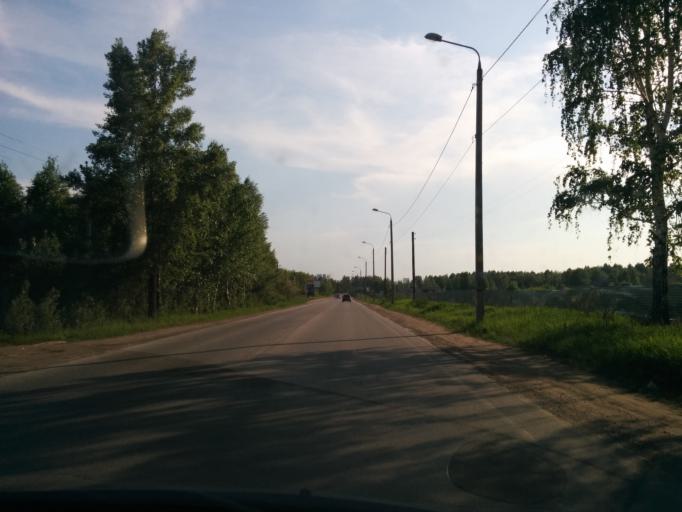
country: RU
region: Perm
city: Perm
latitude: 58.0396
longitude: 56.2634
